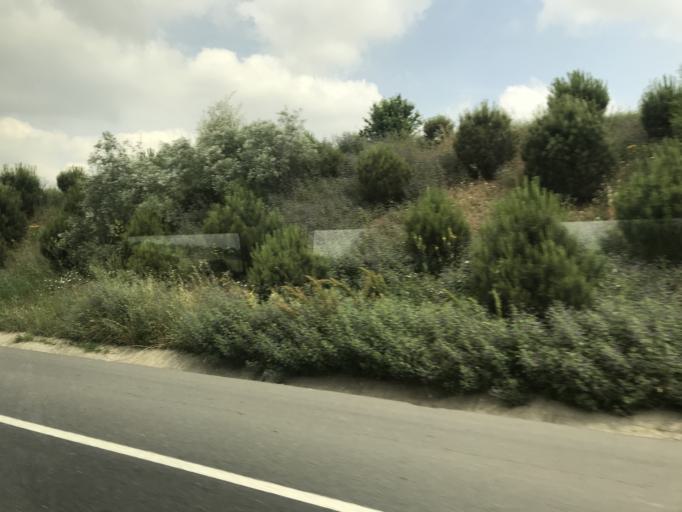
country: TR
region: Tekirdag
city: Tekirdag
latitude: 40.9959
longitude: 27.5567
